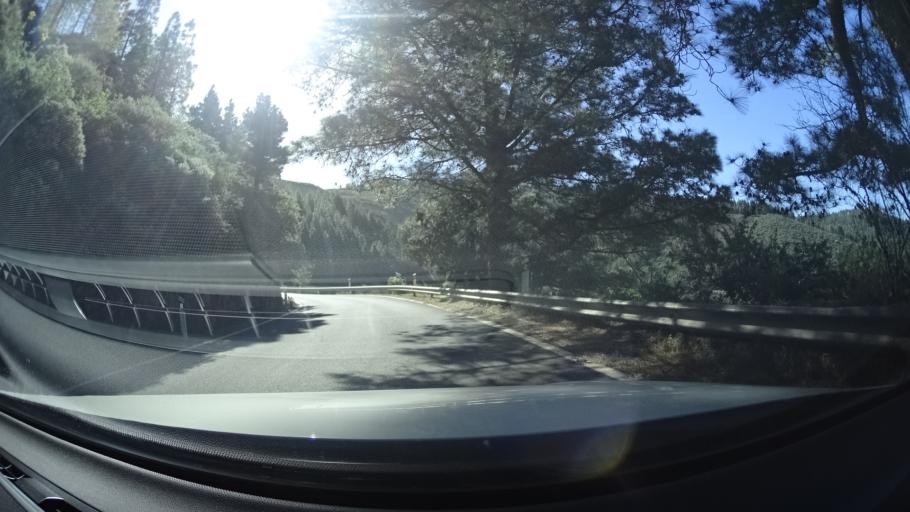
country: ES
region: Canary Islands
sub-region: Provincia de Las Palmas
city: Artenara
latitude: 28.0297
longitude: -15.6196
